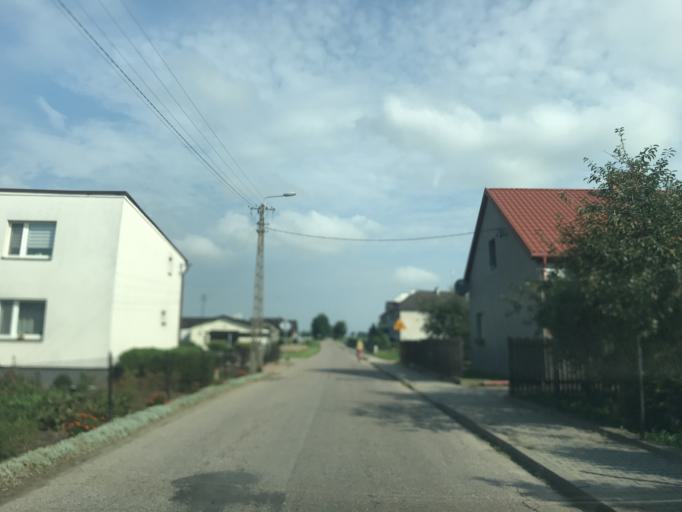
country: PL
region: Kujawsko-Pomorskie
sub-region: Powiat brodnicki
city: Brzozie
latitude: 53.3259
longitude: 19.6064
